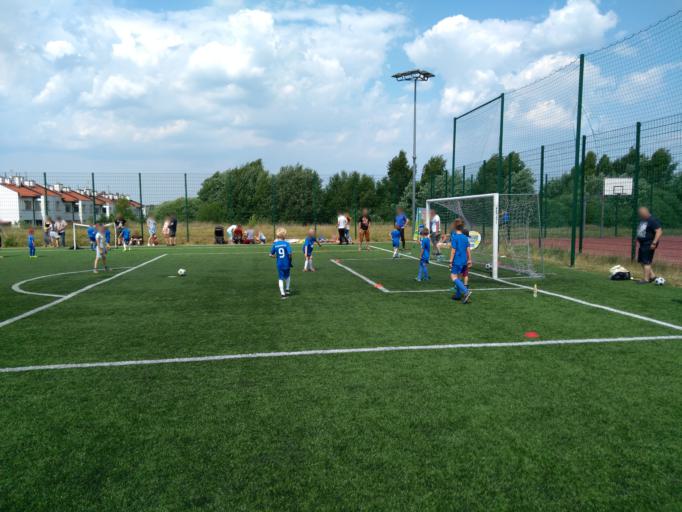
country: PL
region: West Pomeranian Voivodeship
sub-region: Koszalin
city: Koszalin
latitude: 54.2186
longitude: 16.1722
